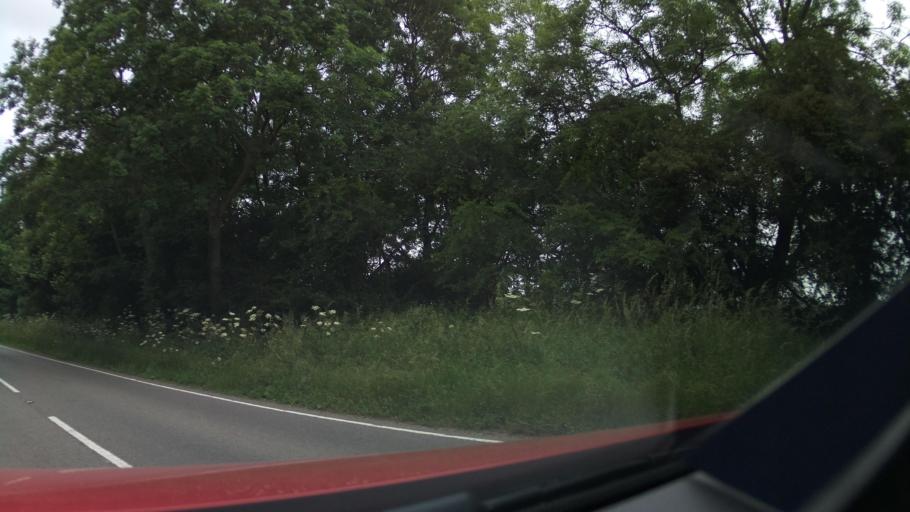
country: GB
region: England
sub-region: Leicestershire
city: Sileby
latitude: 52.8057
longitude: -1.0681
